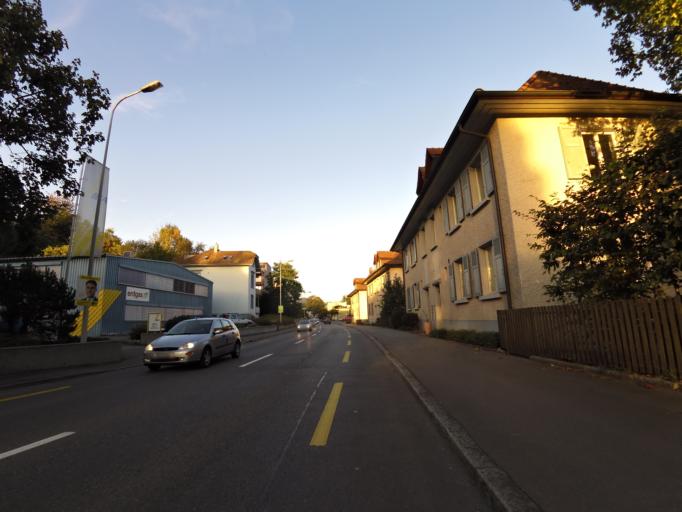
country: CH
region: Aargau
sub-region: Bezirk Aarau
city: Aarau
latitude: 47.3959
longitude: 8.0373
